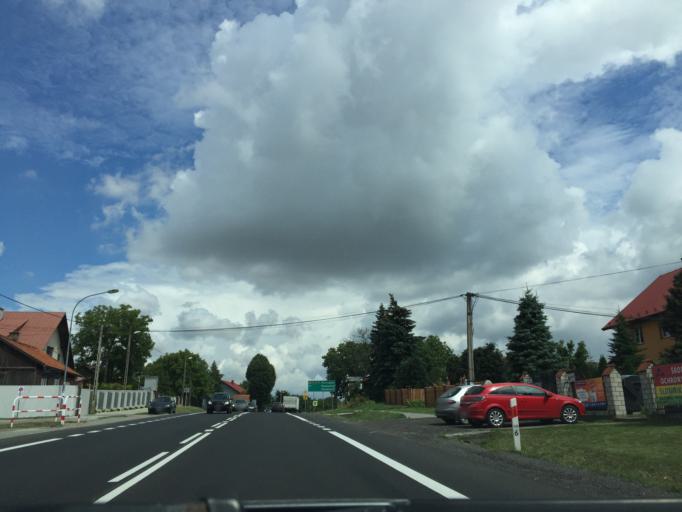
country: PL
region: Lesser Poland Voivodeship
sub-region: Powiat krakowski
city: Michalowice
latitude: 50.2024
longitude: 20.0119
